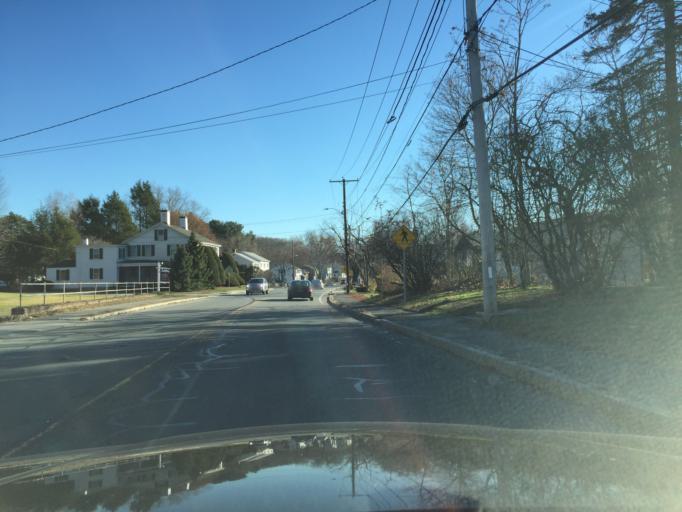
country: US
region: Massachusetts
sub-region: Middlesex County
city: Woburn
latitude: 42.4654
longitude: -71.1757
